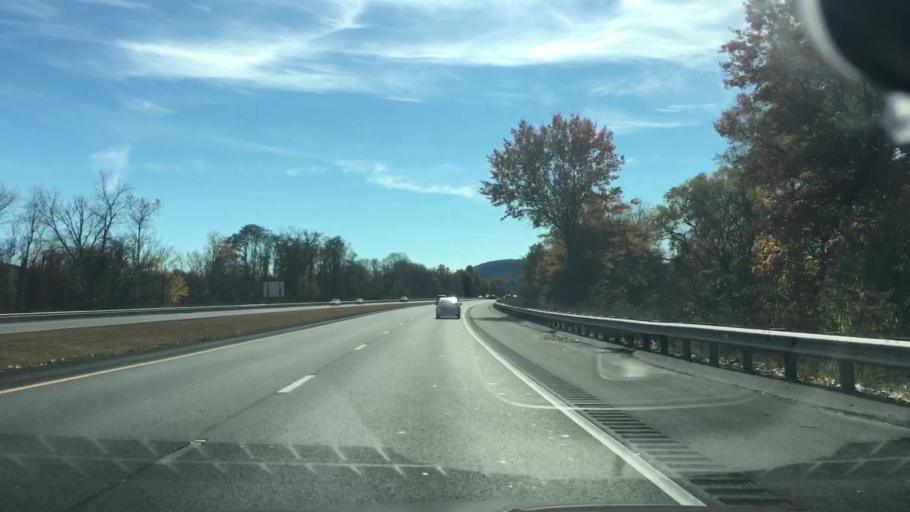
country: US
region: Massachusetts
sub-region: Hampshire County
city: Northampton
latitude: 42.3225
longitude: -72.6156
